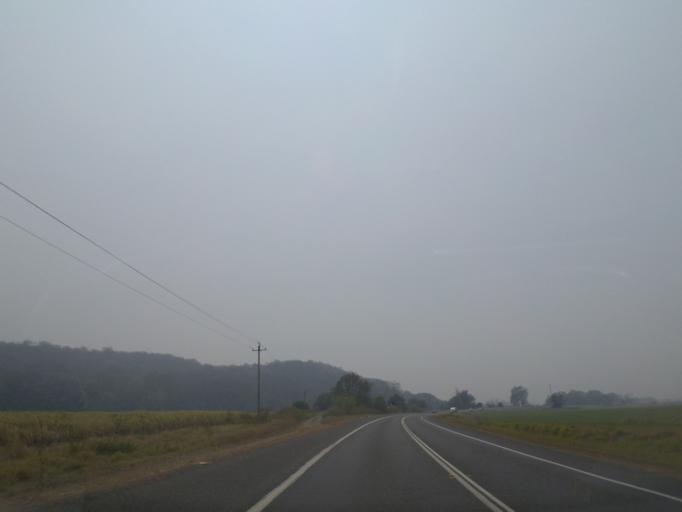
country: AU
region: New South Wales
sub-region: Clarence Valley
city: Maclean
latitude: -29.5418
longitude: 153.1580
